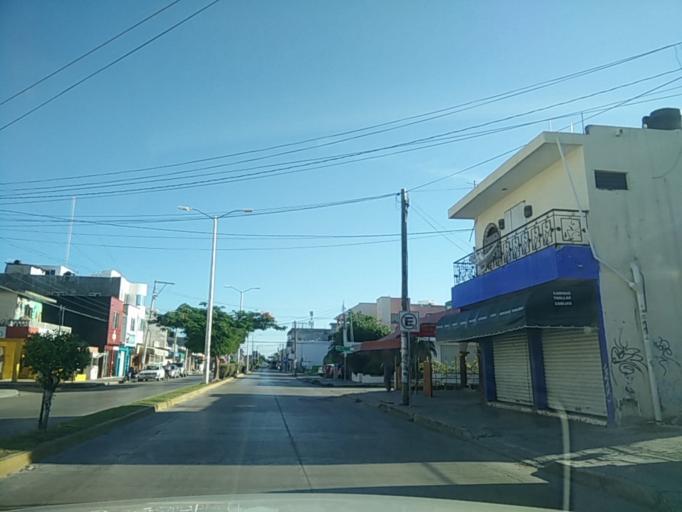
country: MX
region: Quintana Roo
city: Playa del Carmen
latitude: 20.6341
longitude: -87.0736
